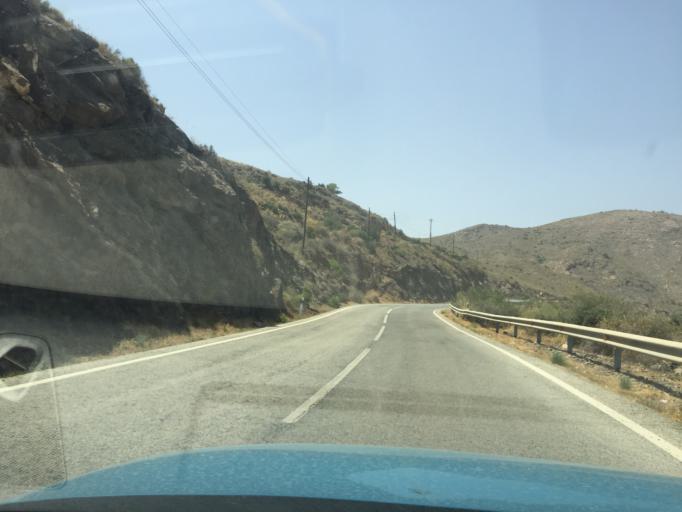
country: ES
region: Murcia
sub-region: Murcia
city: La Union
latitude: 37.5852
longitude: -0.8681
